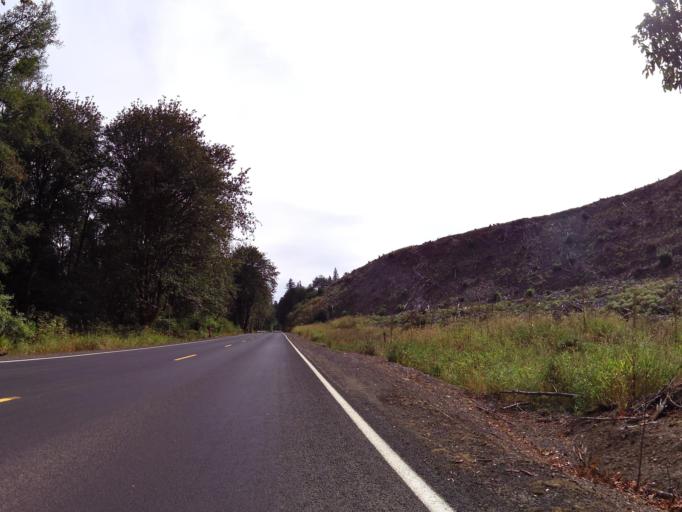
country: US
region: Washington
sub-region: Cowlitz County
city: Castle Rock
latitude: 46.3438
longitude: -122.9392
